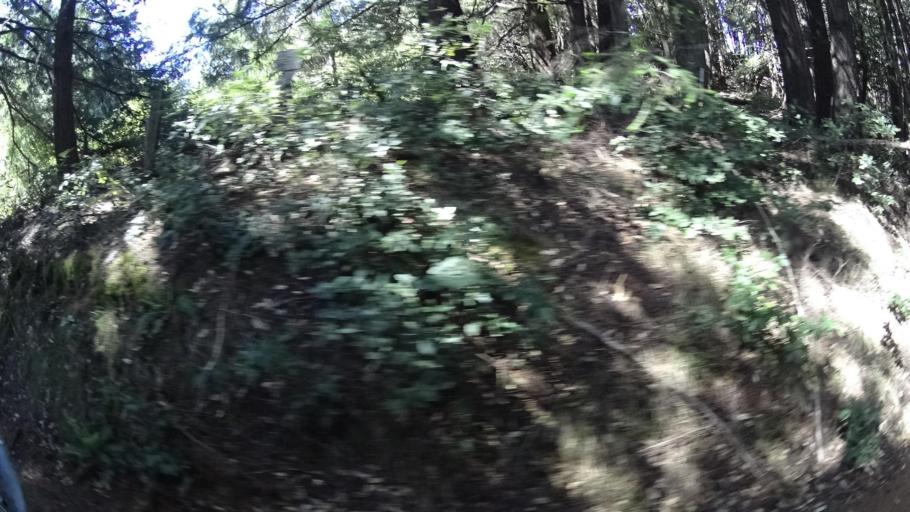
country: US
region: California
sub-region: Humboldt County
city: Redway
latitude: 40.1867
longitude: -124.0926
